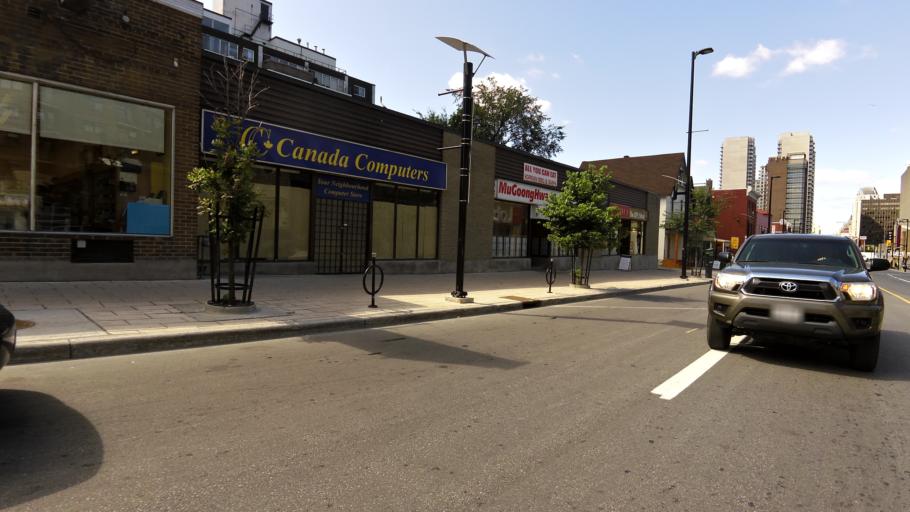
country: CA
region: Ontario
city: Ottawa
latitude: 45.4300
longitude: -75.6828
